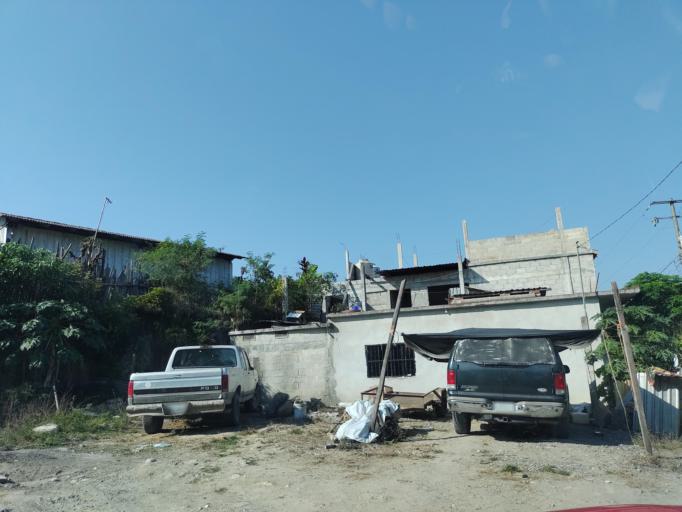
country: MX
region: Veracruz
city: Agua Dulce
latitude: 20.2516
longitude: -97.2540
